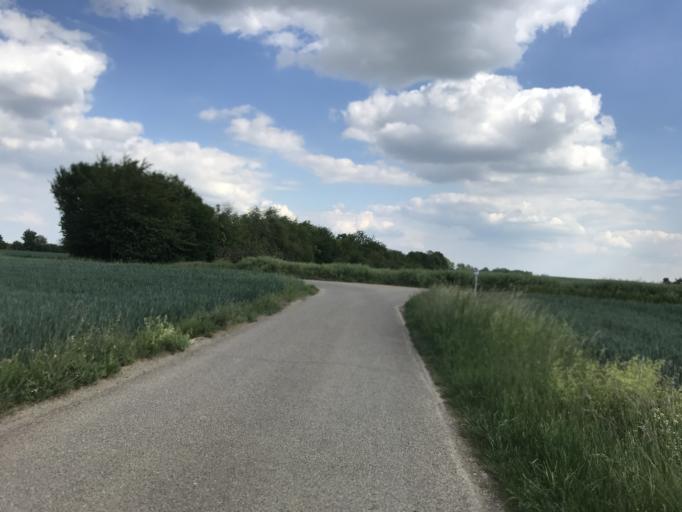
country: DE
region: Rheinland-Pfalz
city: Nieder-Ingelheim
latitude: 49.9735
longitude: 8.0934
